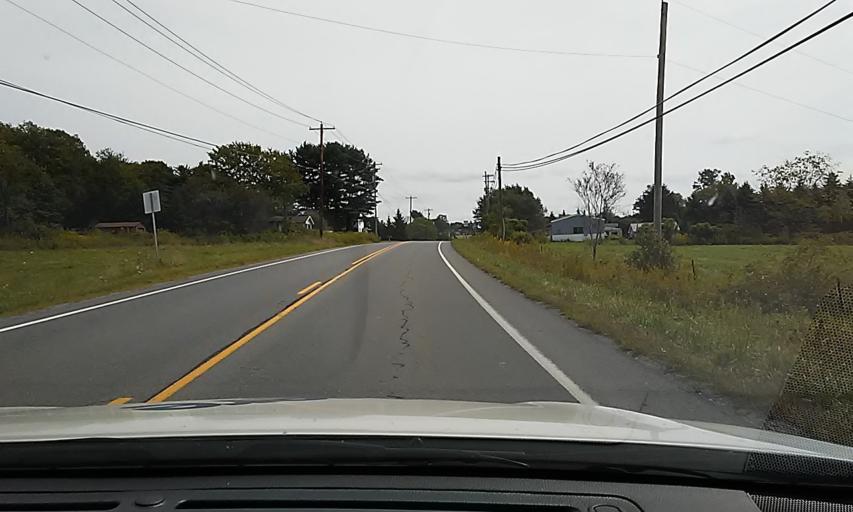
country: US
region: Pennsylvania
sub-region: Elk County
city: Saint Marys
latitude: 41.3623
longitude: -78.5821
